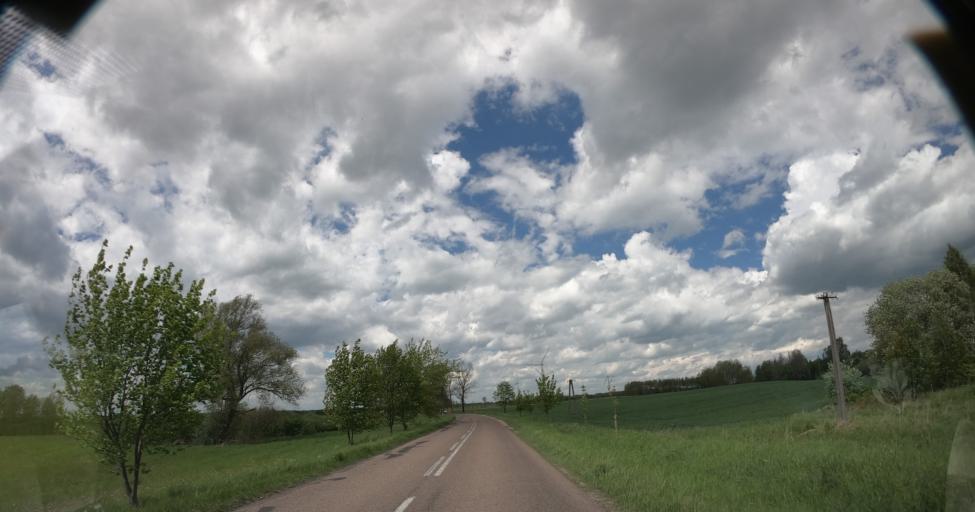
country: PL
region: West Pomeranian Voivodeship
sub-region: Powiat drawski
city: Drawsko Pomorskie
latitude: 53.5445
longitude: 15.7919
